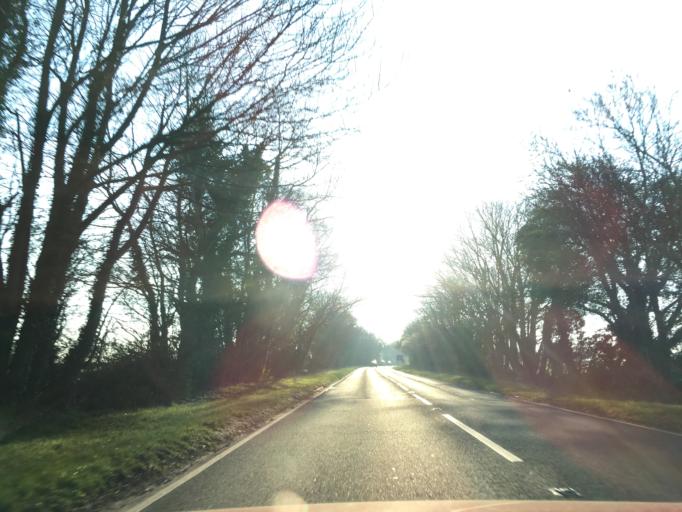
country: GB
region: England
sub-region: Gloucestershire
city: Northleach
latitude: 51.8257
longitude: -1.7969
